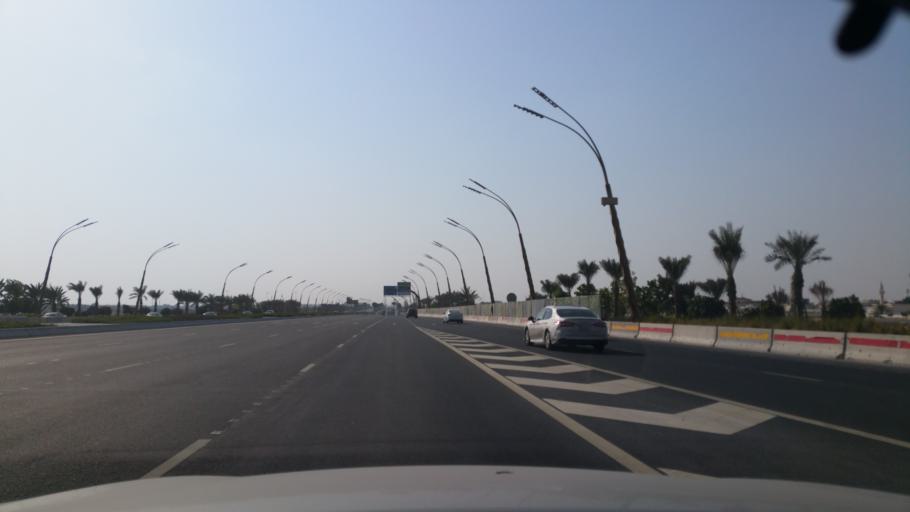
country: QA
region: Baladiyat ar Rayyan
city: Ar Rayyan
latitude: 25.3098
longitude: 51.4002
